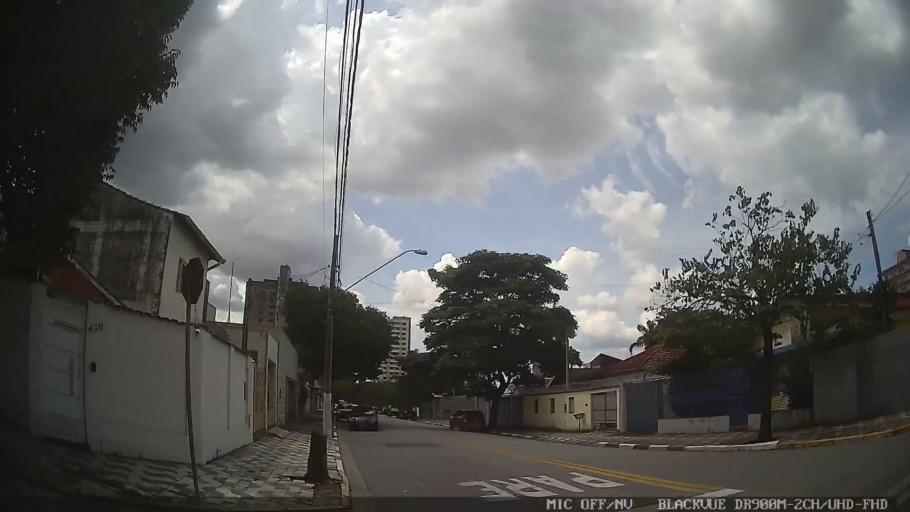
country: BR
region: Sao Paulo
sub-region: Suzano
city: Suzano
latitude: -23.5442
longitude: -46.3080
